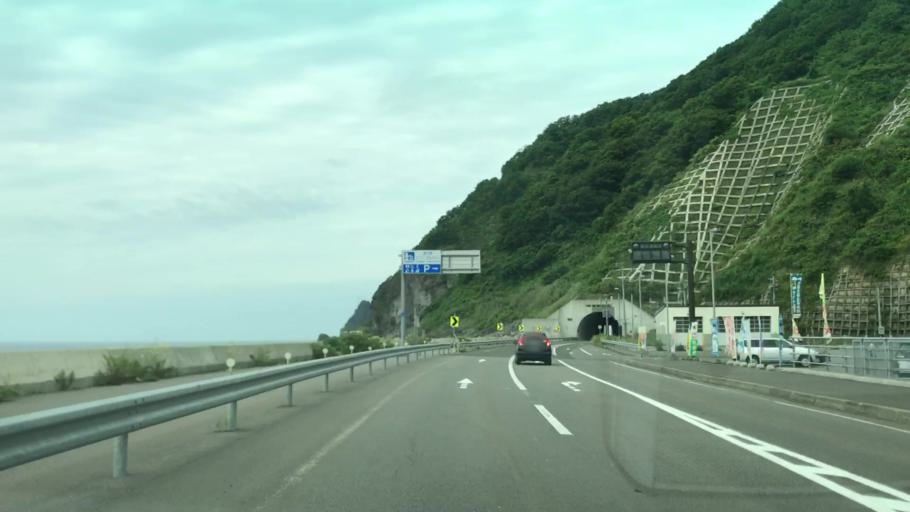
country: JP
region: Hokkaido
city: Iwanai
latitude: 43.1648
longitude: 140.3855
